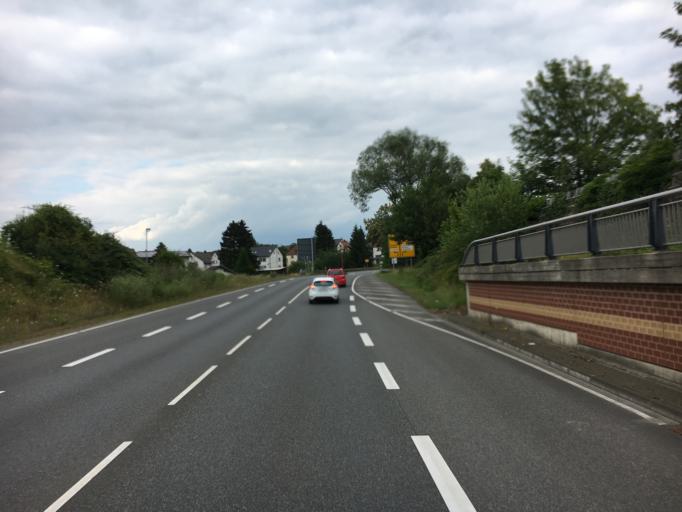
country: DE
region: Hesse
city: Stadtallendorf
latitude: 50.8312
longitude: 9.0100
